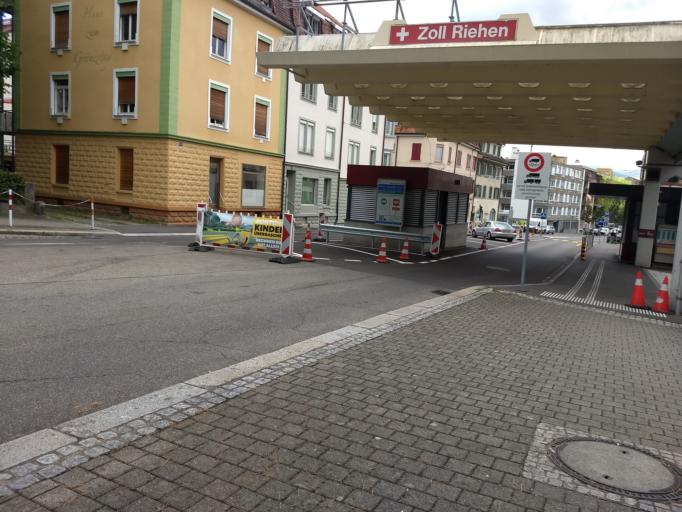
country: CH
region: Basel-City
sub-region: Basel-Stadt
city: Riehen
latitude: 47.5955
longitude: 7.6555
